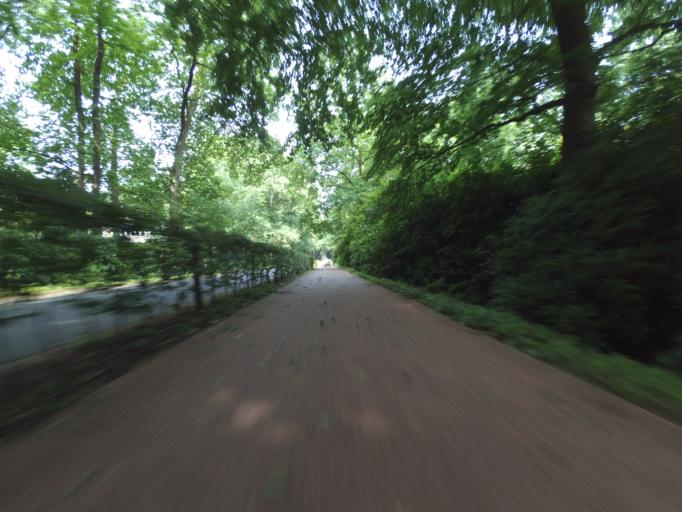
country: BE
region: Flanders
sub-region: Provincie Antwerpen
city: Kalmthout
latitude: 51.3580
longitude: 4.4670
